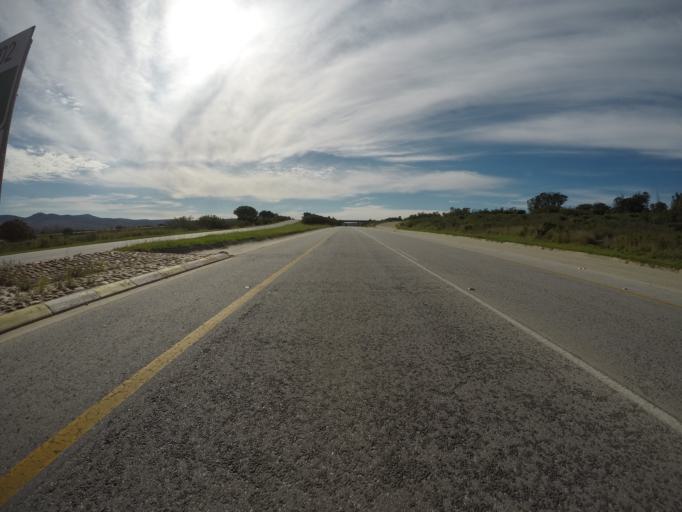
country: ZA
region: Eastern Cape
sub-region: Cacadu District Municipality
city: Jeffrey's Bay
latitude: -33.8987
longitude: 25.1182
